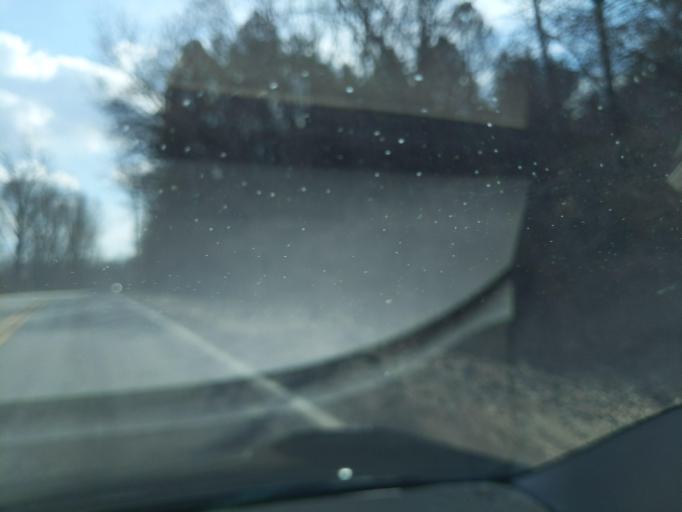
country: US
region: Michigan
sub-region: Washtenaw County
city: Chelsea
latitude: 42.3976
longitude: -84.0382
